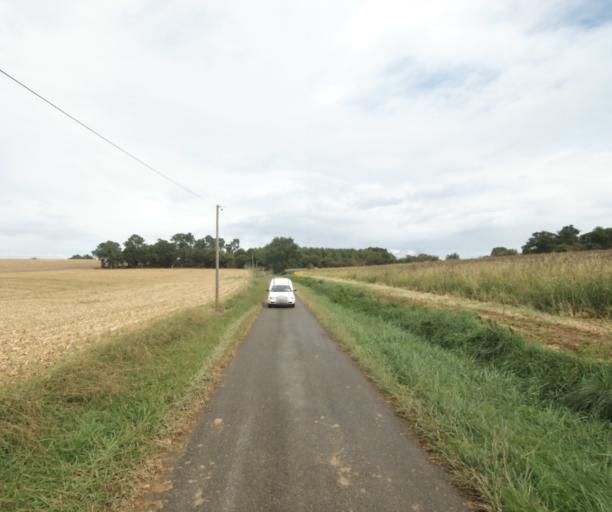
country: FR
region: Midi-Pyrenees
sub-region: Departement du Gers
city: Cazaubon
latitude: 43.9001
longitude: -0.1337
